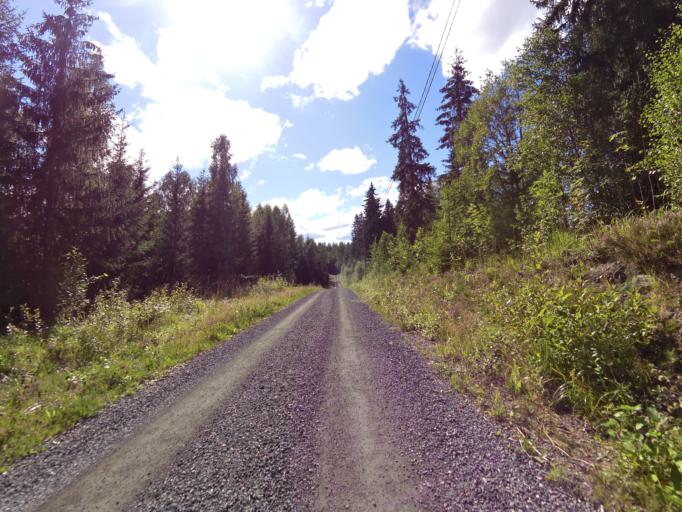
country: SE
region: Gaevleborg
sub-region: Hofors Kommun
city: Hofors
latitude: 60.5335
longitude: 16.2420
